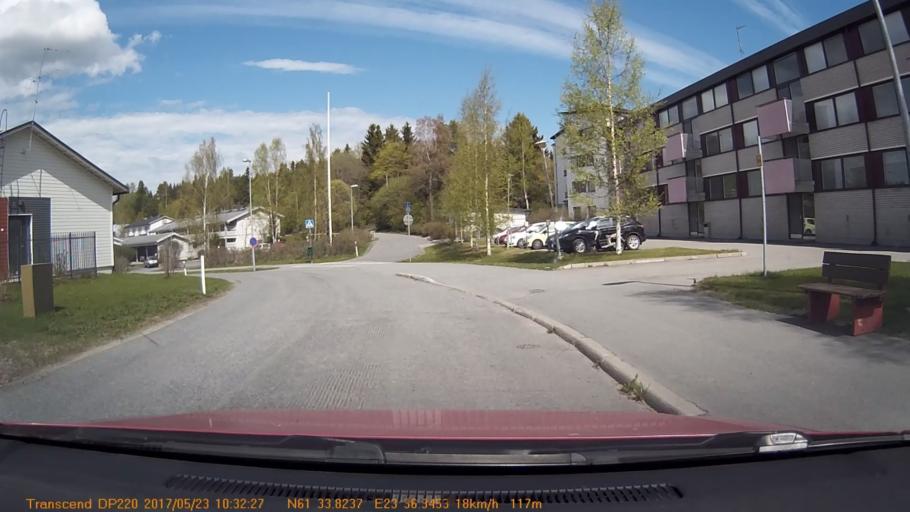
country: FI
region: Pirkanmaa
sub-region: Tampere
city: Yloejaervi
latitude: 61.5639
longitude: 23.6058
